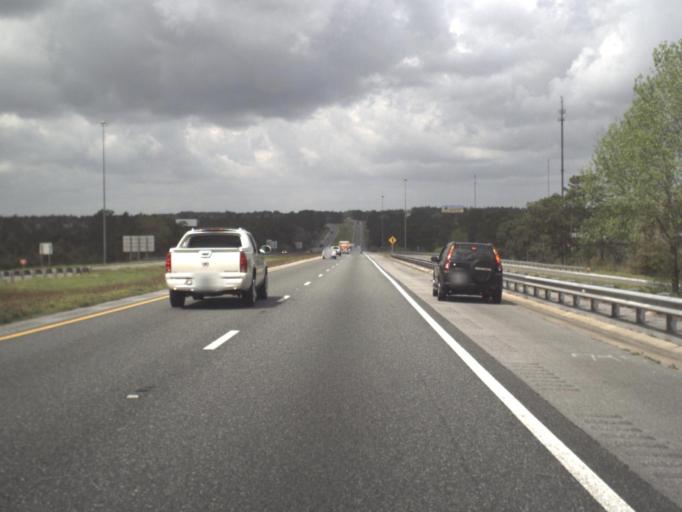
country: US
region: Florida
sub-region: Okaloosa County
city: Crestview
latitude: 30.7258
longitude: -86.5692
